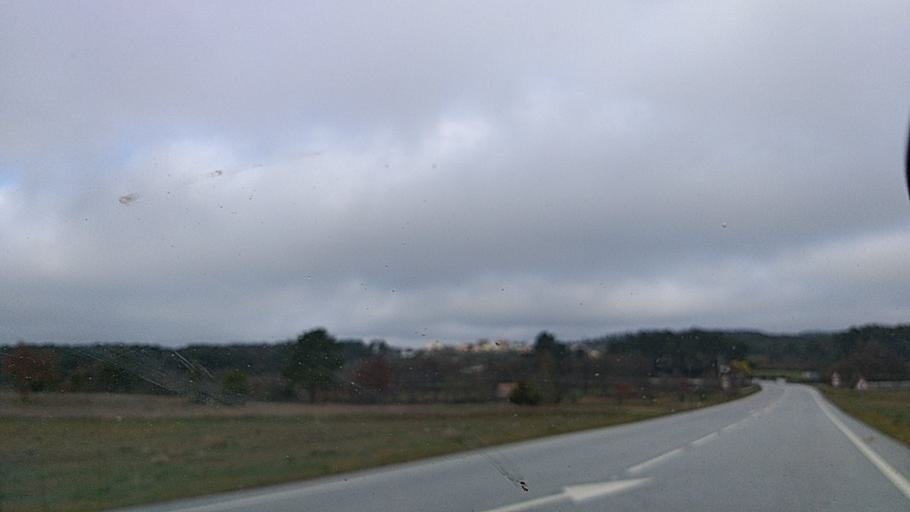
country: PT
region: Guarda
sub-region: Fornos de Algodres
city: Fornos de Algodres
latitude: 40.7163
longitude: -7.4873
